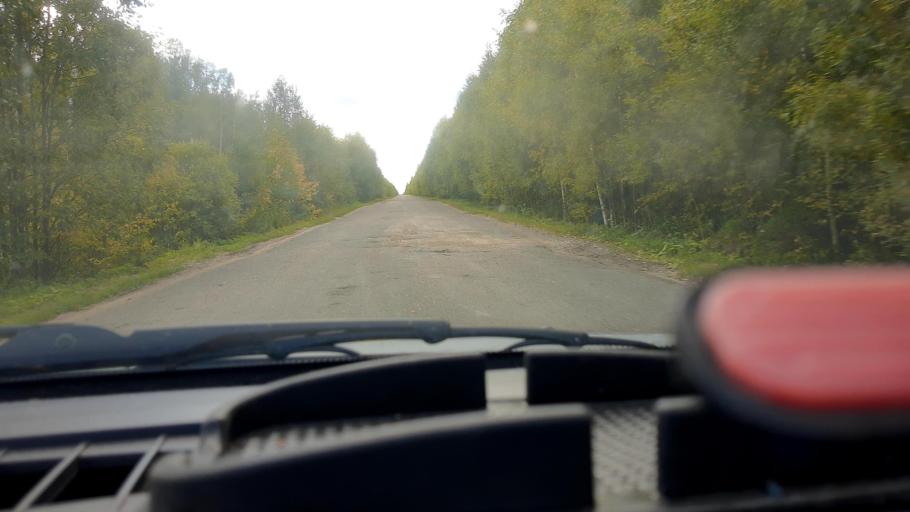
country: RU
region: Mariy-El
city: Kilemary
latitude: 56.9054
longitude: 46.7365
